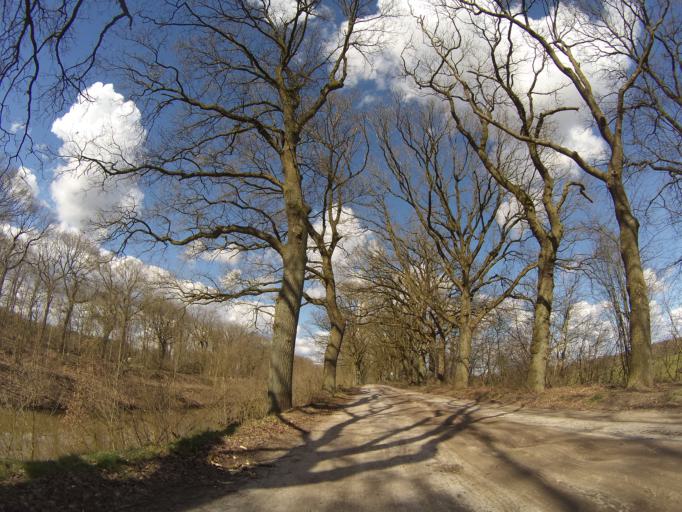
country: NL
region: Drenthe
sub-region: Gemeente Emmen
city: Emmen
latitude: 52.7763
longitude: 6.8761
